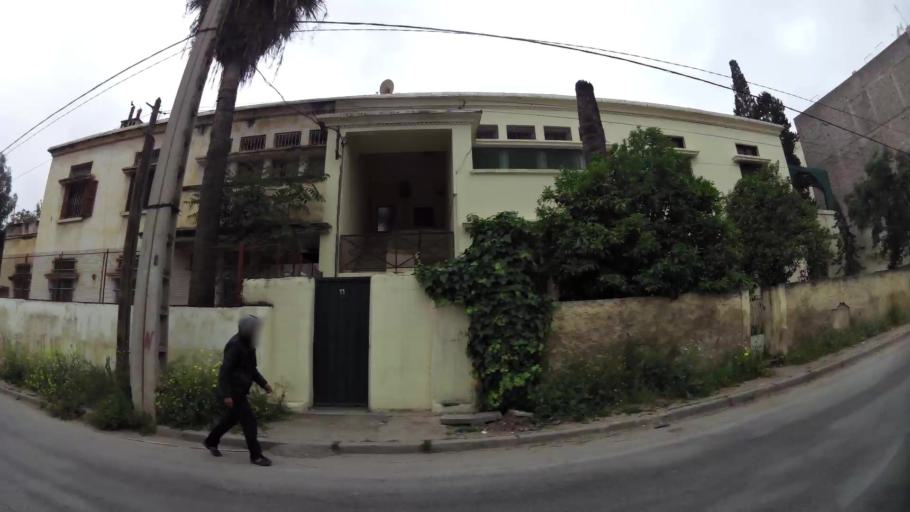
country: MA
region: Fes-Boulemane
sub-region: Fes
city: Fes
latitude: 34.0337
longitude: -4.9920
